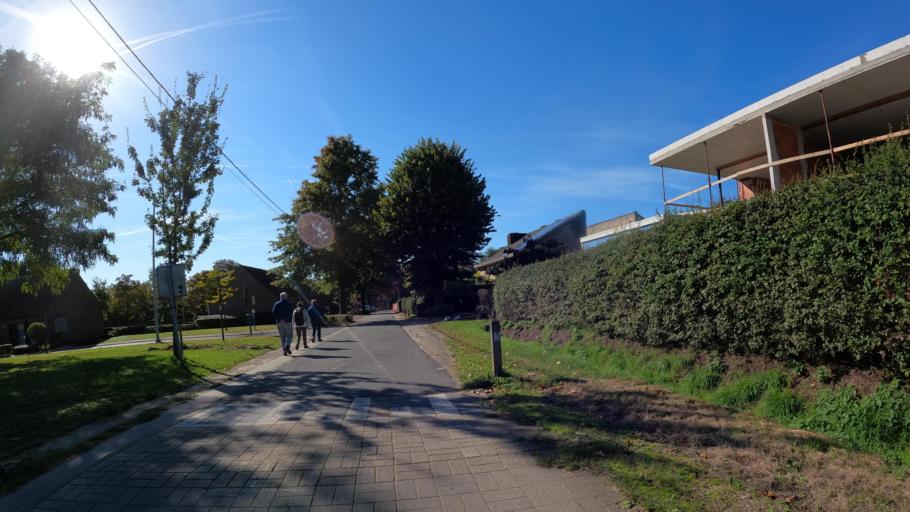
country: BE
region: Flanders
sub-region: Provincie Oost-Vlaanderen
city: Waasmunster
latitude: 51.1146
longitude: 4.0881
